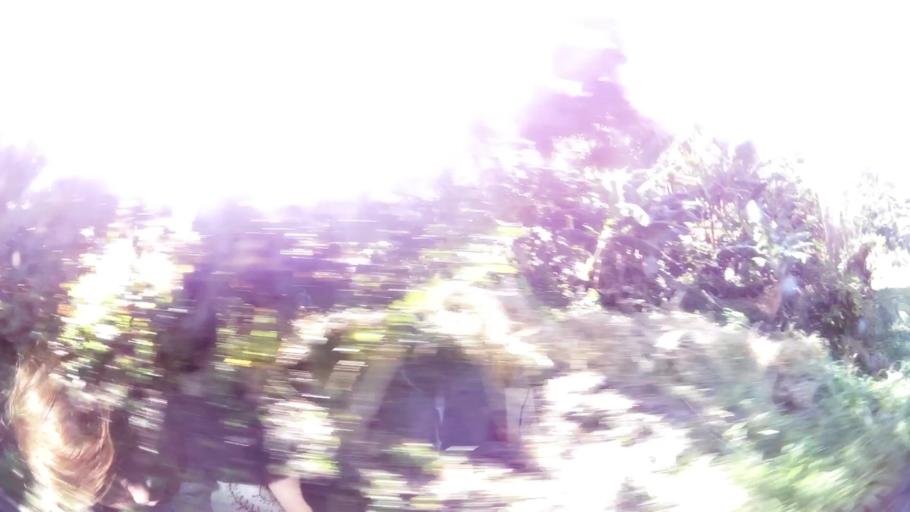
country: DM
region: Saint Paul
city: Mahaut
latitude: 15.3417
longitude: -61.3769
